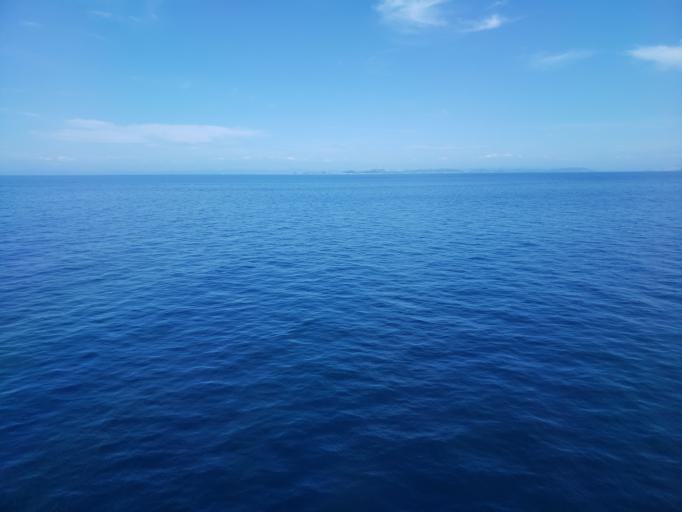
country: JP
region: Hyogo
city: Fukura
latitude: 34.4807
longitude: 134.5286
